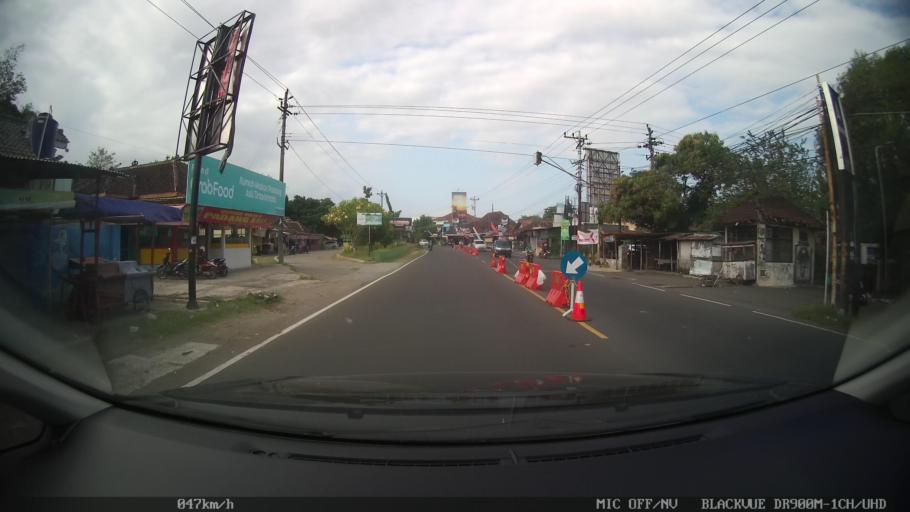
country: ID
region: Daerah Istimewa Yogyakarta
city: Kasihan
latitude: -7.8389
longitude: 110.3504
